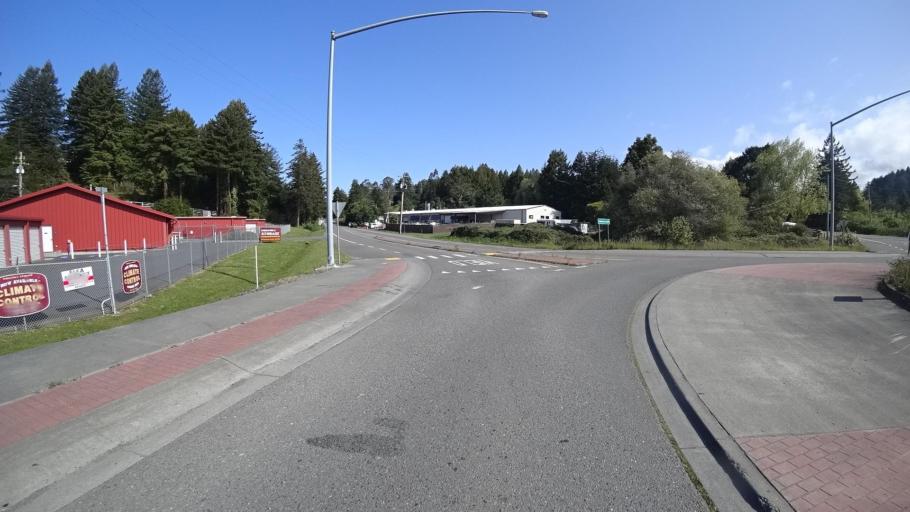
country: US
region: California
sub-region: Humboldt County
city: Bayside
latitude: 40.8105
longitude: -124.0863
